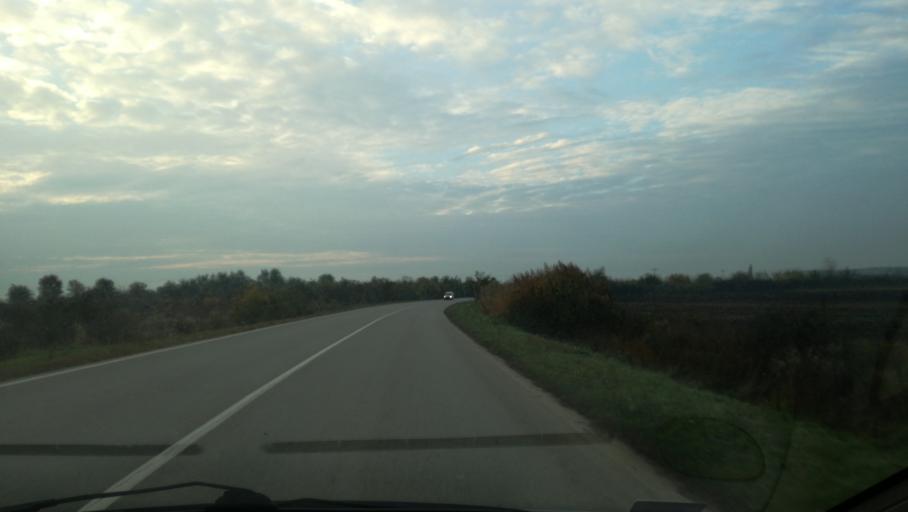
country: RS
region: Autonomna Pokrajina Vojvodina
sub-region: Severnobanatski Okrug
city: Kikinda
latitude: 45.8011
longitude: 20.4384
